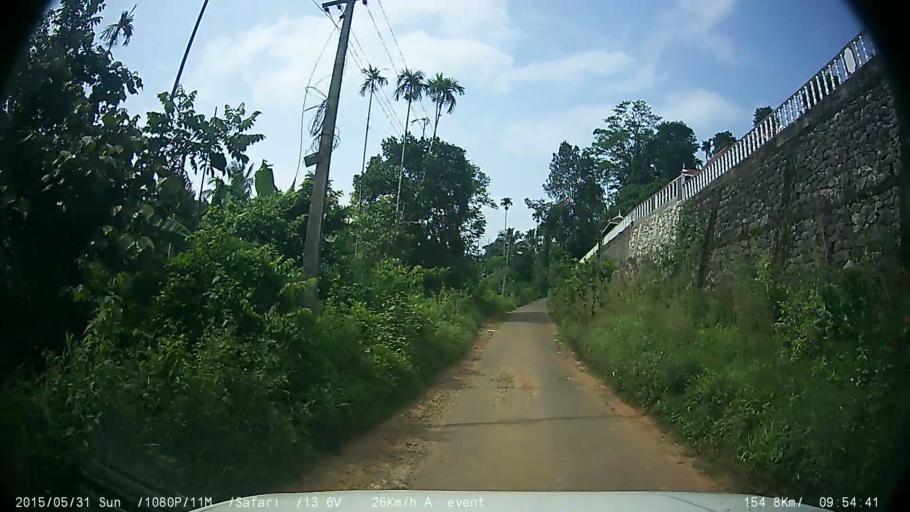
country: IN
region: Kerala
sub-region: Wayanad
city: Kalpetta
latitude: 11.6056
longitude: 76.0534
